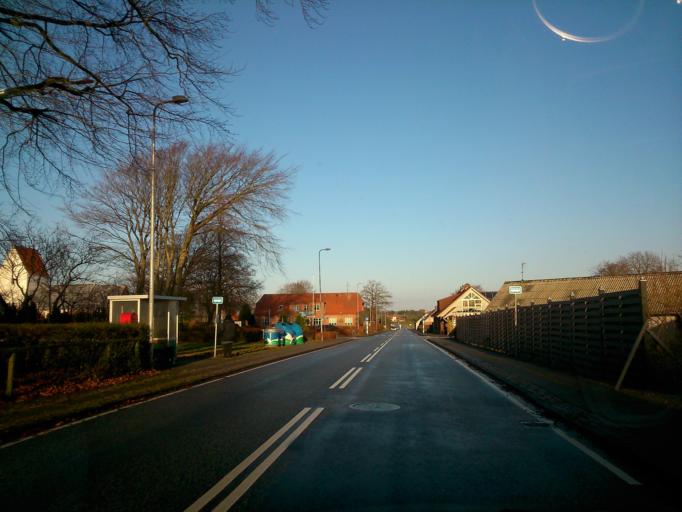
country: DK
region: Central Jutland
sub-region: Ringkobing-Skjern Kommune
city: Tarm
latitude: 55.9851
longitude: 8.5927
